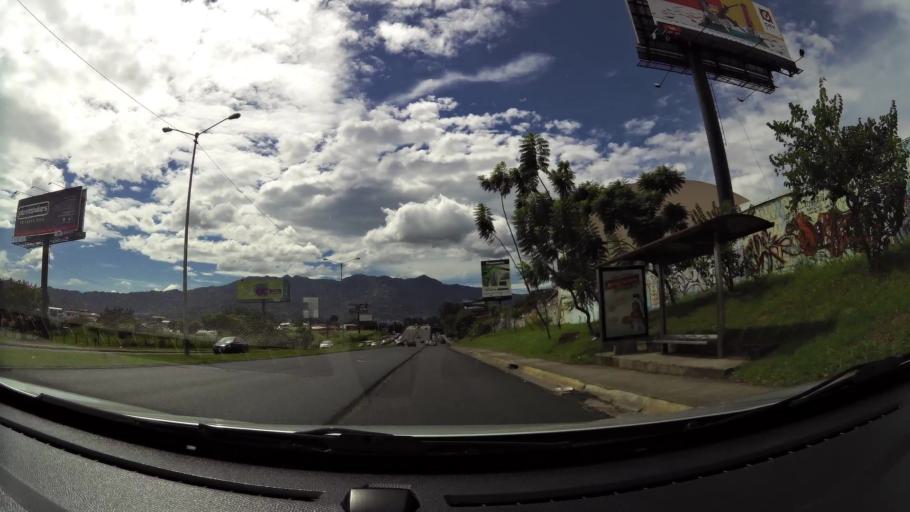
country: CR
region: San Jose
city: San Pedro
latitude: 9.9170
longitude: -84.0656
